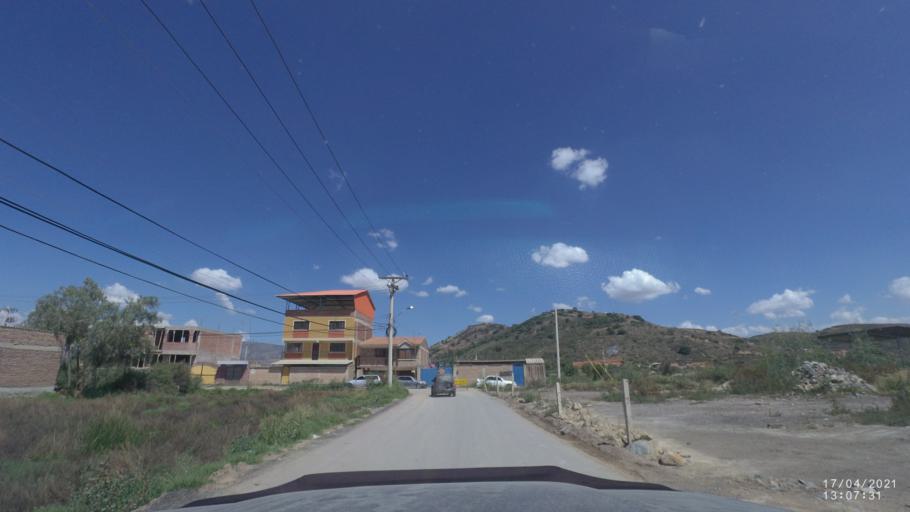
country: BO
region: Cochabamba
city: Cochabamba
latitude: -17.4137
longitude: -66.2240
